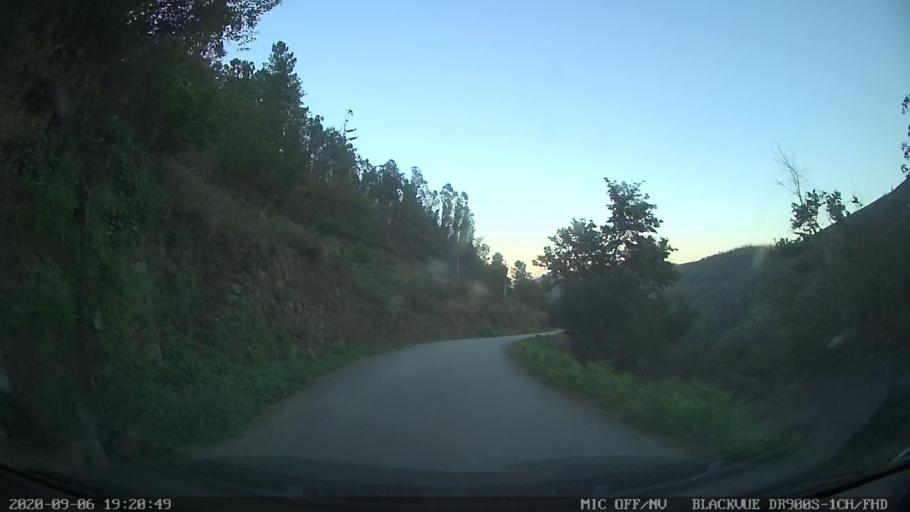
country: PT
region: Porto
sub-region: Baiao
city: Valadares
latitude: 41.1863
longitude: -7.9371
